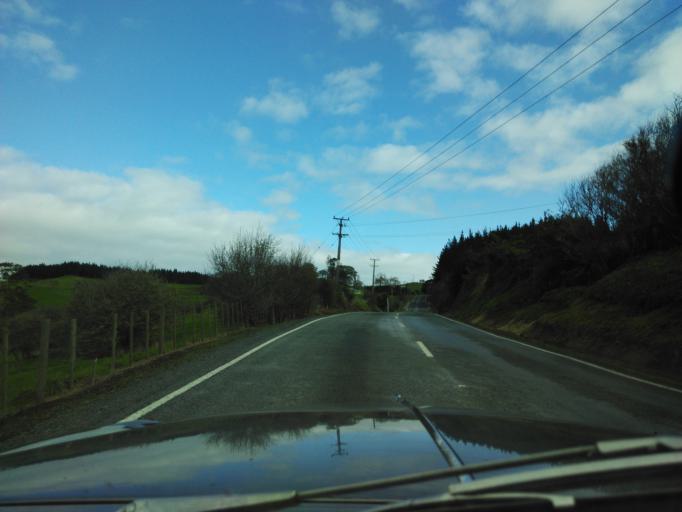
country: NZ
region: Auckland
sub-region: Auckland
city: Wellsford
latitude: -36.2840
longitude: 174.4446
